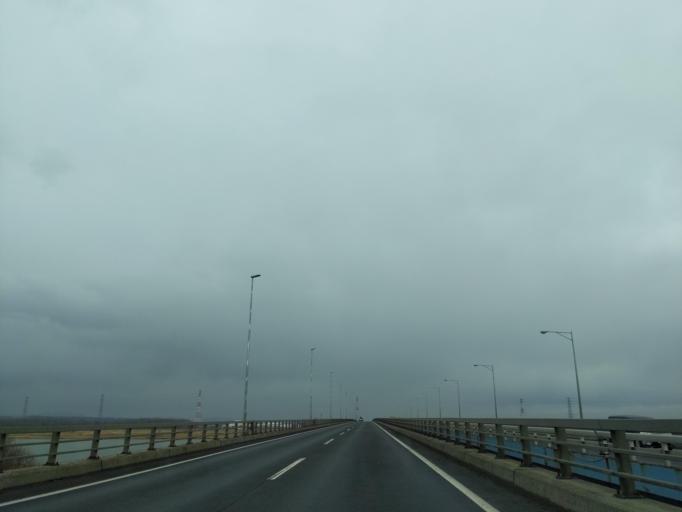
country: JP
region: Hokkaido
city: Ishikari
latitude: 43.1711
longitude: 141.4159
